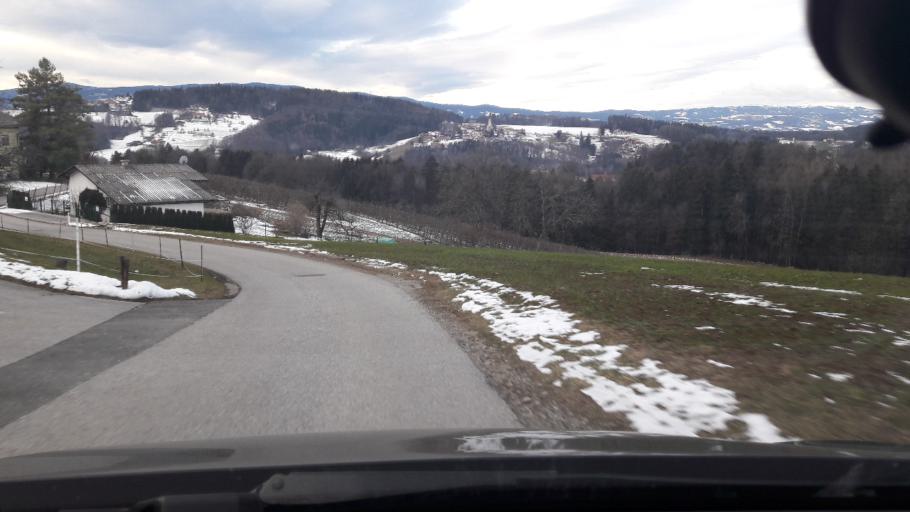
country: AT
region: Styria
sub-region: Politischer Bezirk Graz-Umgebung
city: Sankt Oswald bei Plankenwarth
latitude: 47.0781
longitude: 15.2754
